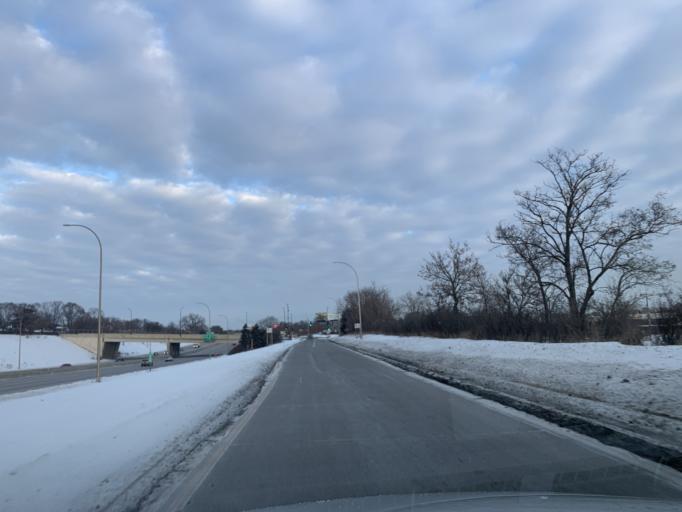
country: US
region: Minnesota
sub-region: Anoka County
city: Columbia Heights
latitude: 45.0221
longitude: -93.2830
